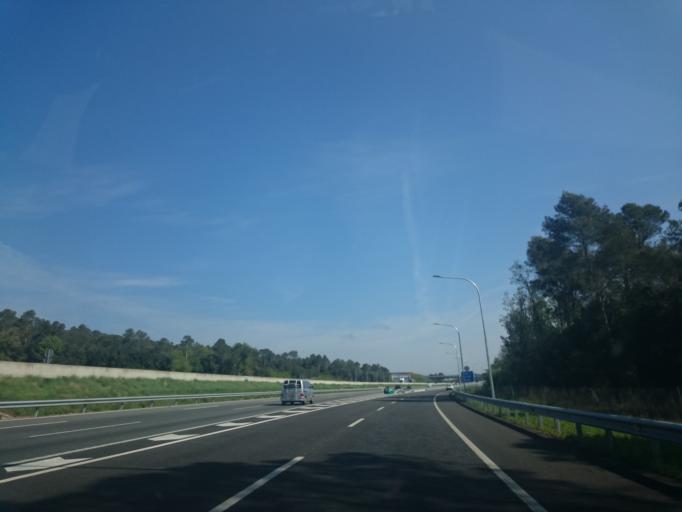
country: ES
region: Catalonia
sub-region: Provincia de Girona
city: Cervia de Ter
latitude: 42.0712
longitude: 2.8871
